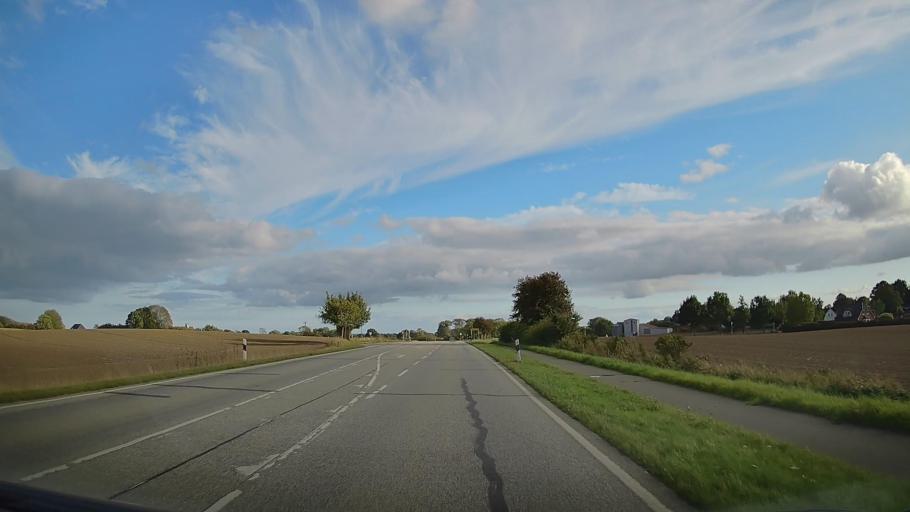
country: DE
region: Schleswig-Holstein
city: Rabel
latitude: 54.7247
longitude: 9.9508
